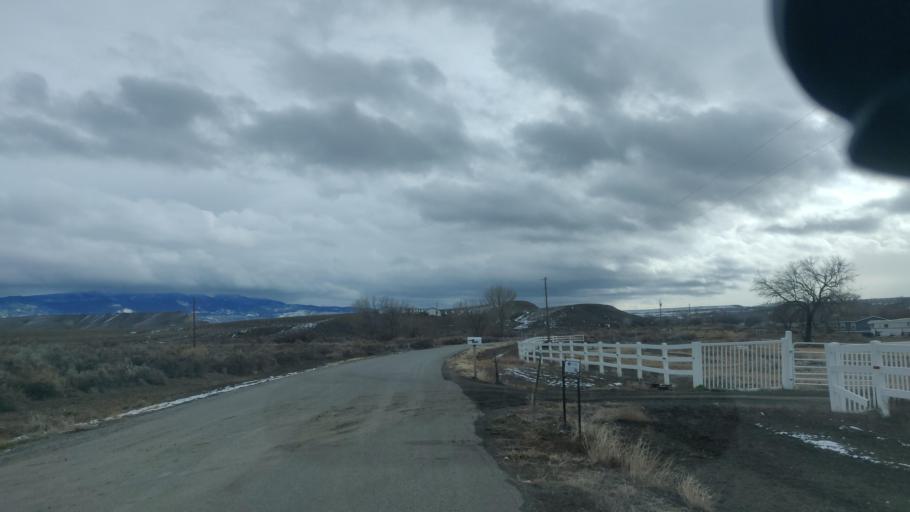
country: US
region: Colorado
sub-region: Mesa County
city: Clifton
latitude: 38.9416
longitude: -108.3977
